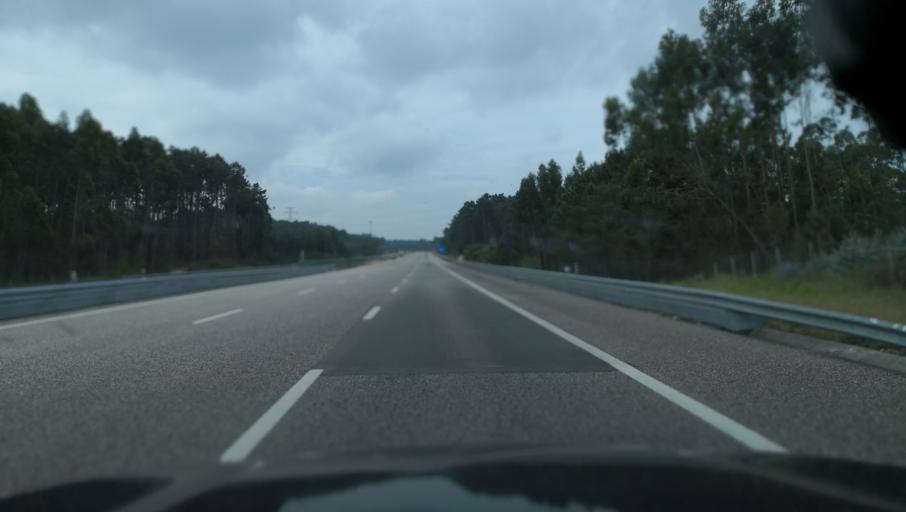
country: PT
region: Leiria
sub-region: Leiria
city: Monte Redondo
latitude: 39.9167
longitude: -8.7969
